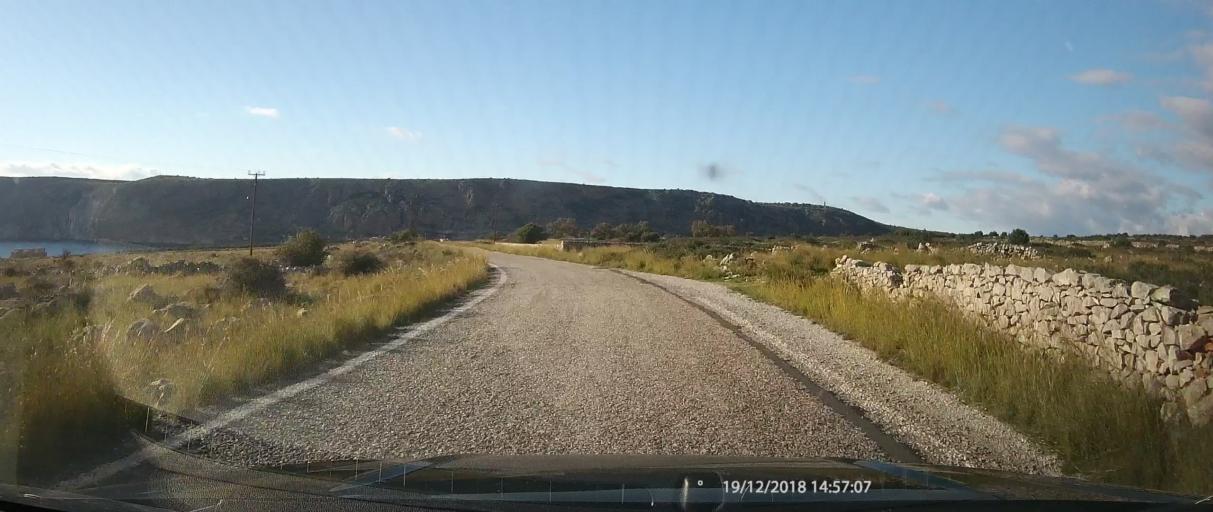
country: GR
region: Peloponnese
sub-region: Nomos Lakonias
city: Gytheio
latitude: 36.4799
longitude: 22.4097
